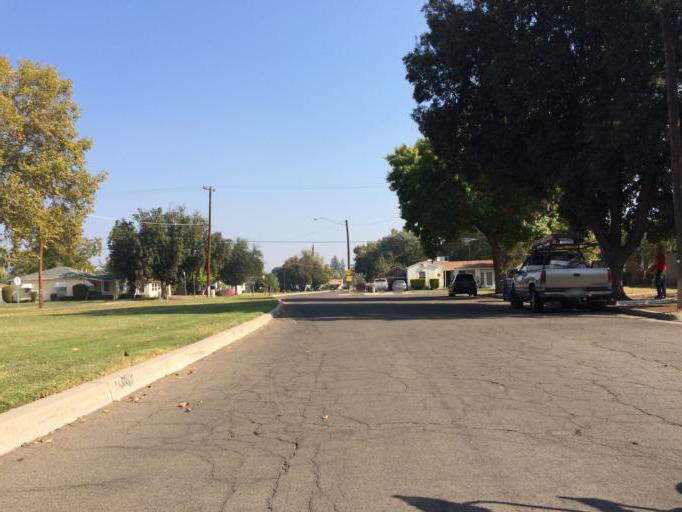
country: US
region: California
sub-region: Fresno County
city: Fresno
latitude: 36.7467
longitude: -119.7439
